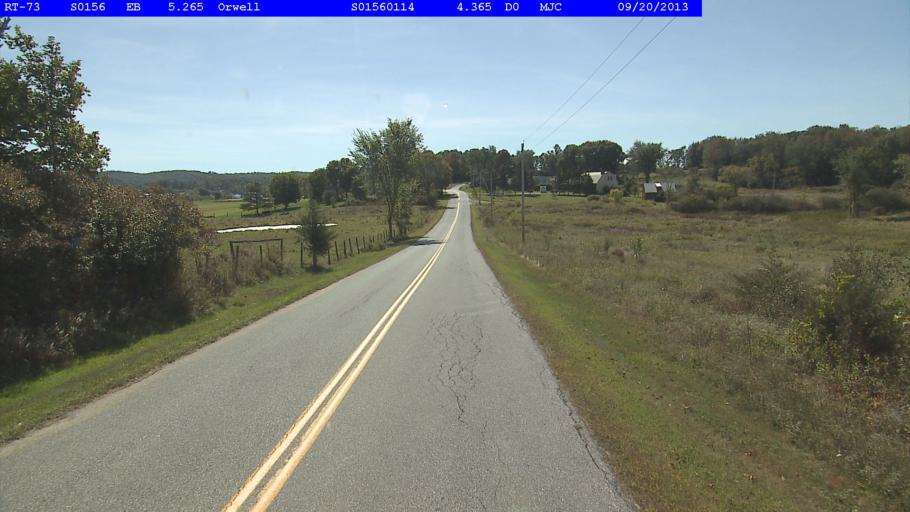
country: US
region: New York
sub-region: Essex County
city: Ticonderoga
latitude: 43.8075
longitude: -73.3123
